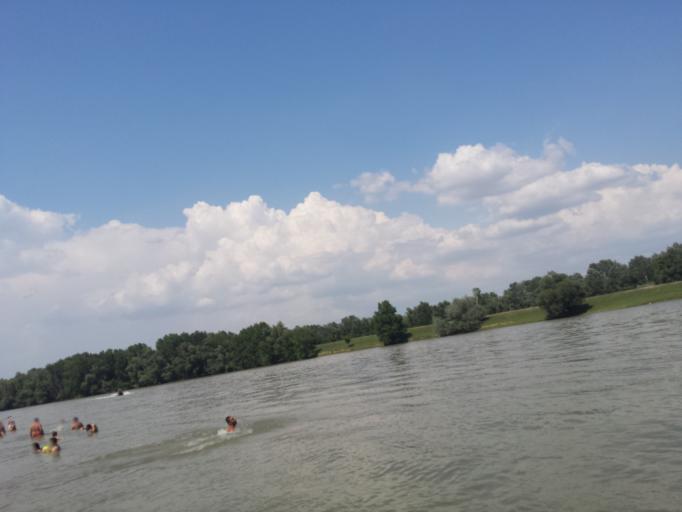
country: RO
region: Calarasi
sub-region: Municipiul Calarasi
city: Calarasi
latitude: 44.1563
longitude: 27.3203
